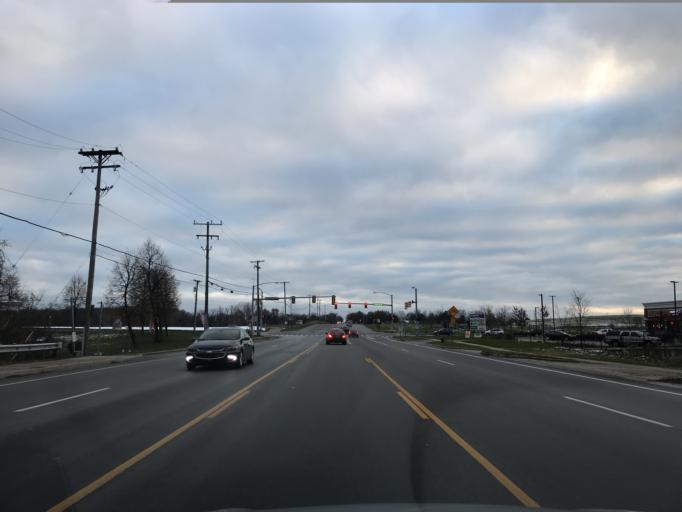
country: US
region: Michigan
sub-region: Washtenaw County
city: Ann Arbor
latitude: 42.2315
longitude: -83.6998
